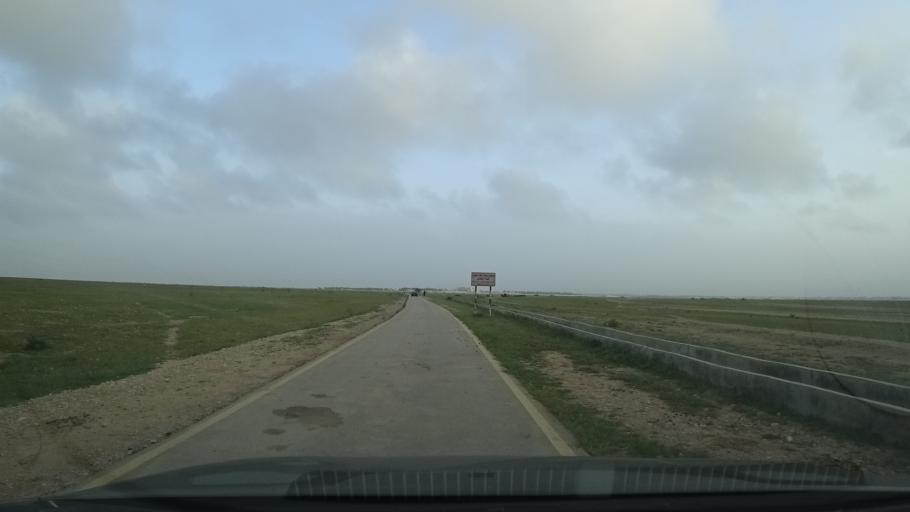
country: OM
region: Zufar
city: Salalah
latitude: 17.0815
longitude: 54.2317
